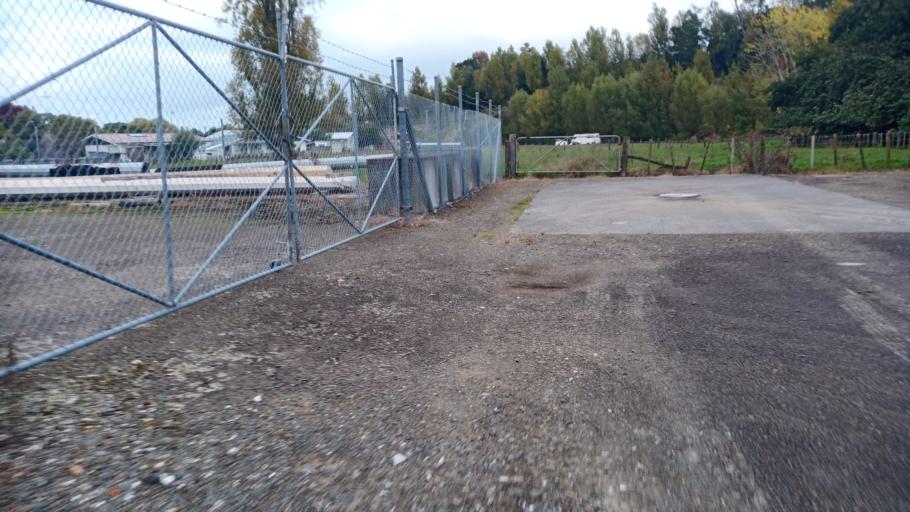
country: NZ
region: Gisborne
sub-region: Gisborne District
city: Gisborne
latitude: -38.6441
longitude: 178.0250
